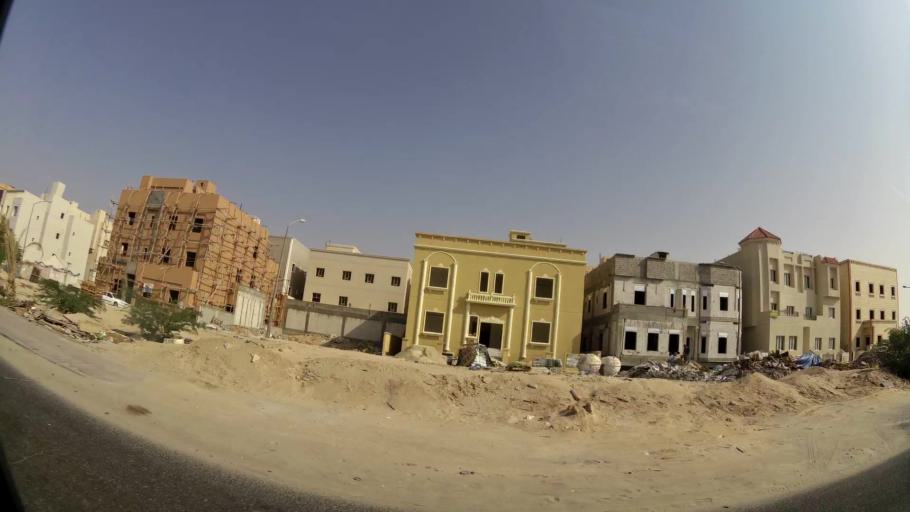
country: KW
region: Muhafazat al Jahra'
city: Al Jahra'
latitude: 29.3171
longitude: 47.6779
